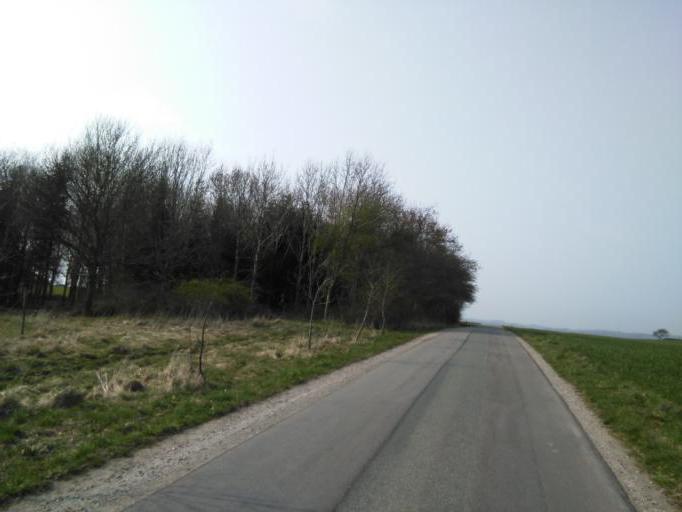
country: DK
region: Central Jutland
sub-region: Arhus Kommune
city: Beder
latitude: 56.0668
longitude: 10.2309
